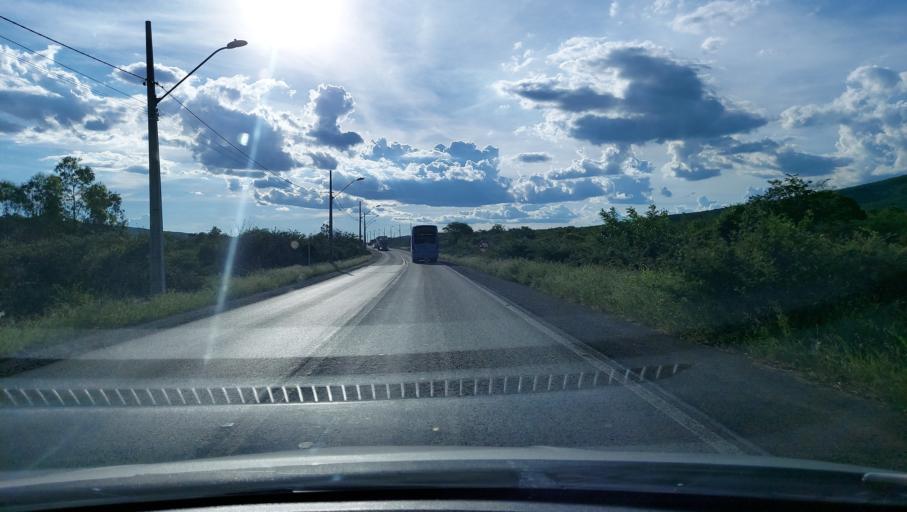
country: BR
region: Bahia
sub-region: Seabra
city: Seabra
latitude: -12.4569
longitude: -42.2167
